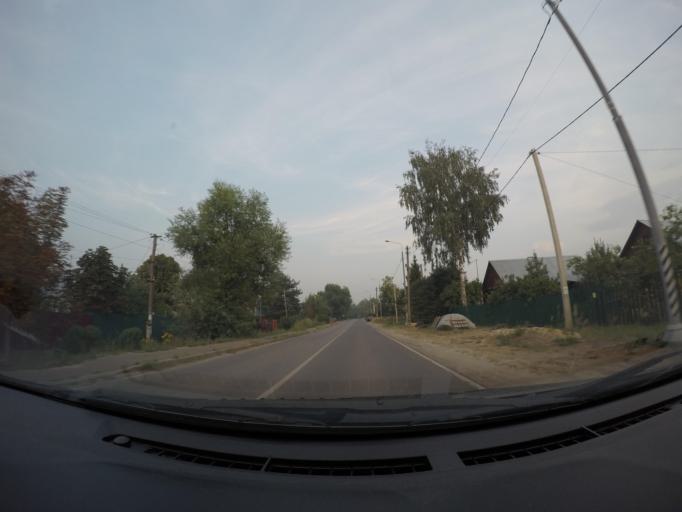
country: RU
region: Moskovskaya
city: Imeni Tsyurupy
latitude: 55.4919
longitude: 38.6735
